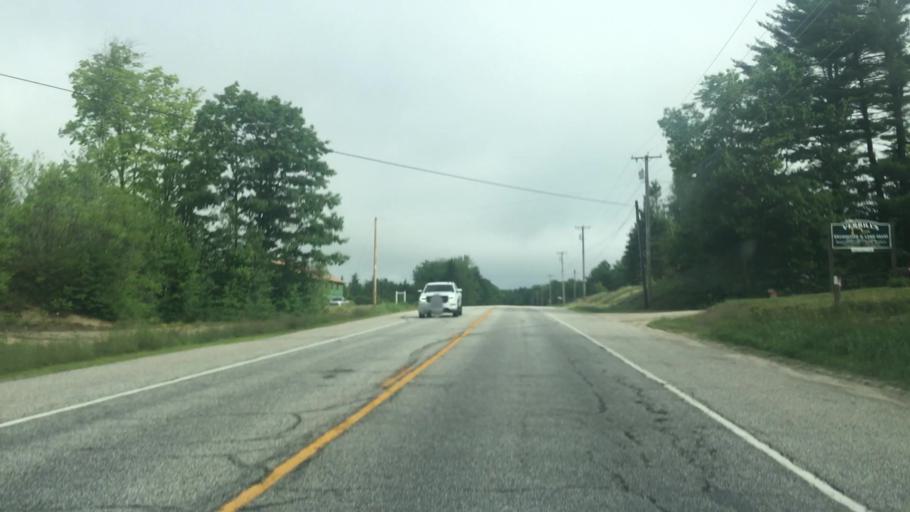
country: US
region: Maine
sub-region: Oxford County
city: Paris
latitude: 44.2545
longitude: -70.5131
